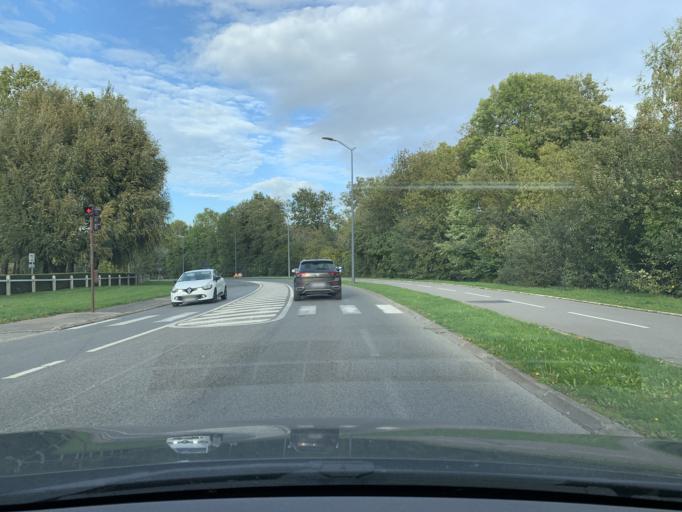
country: FR
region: Picardie
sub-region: Departement de l'Aisne
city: Harly
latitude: 49.8510
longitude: 3.3093
